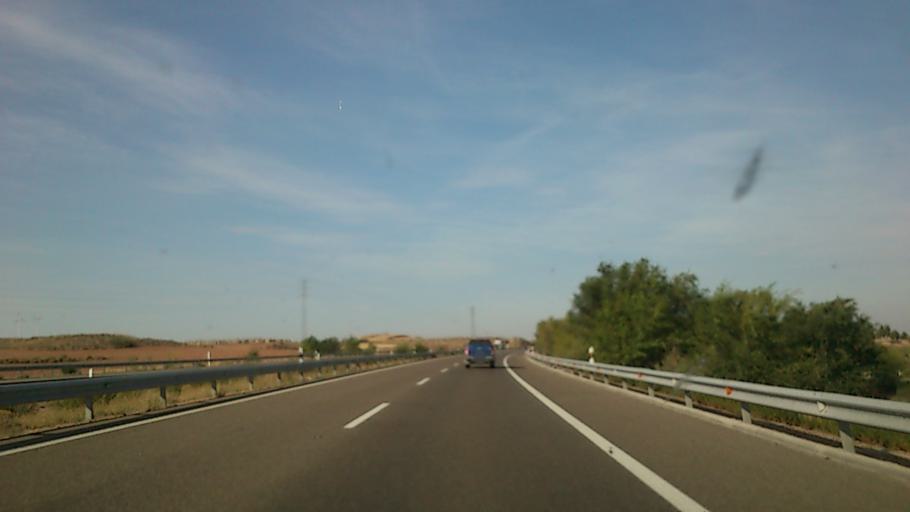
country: ES
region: Aragon
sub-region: Provincia de Zaragoza
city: Longares
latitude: 41.4429
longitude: -1.1407
